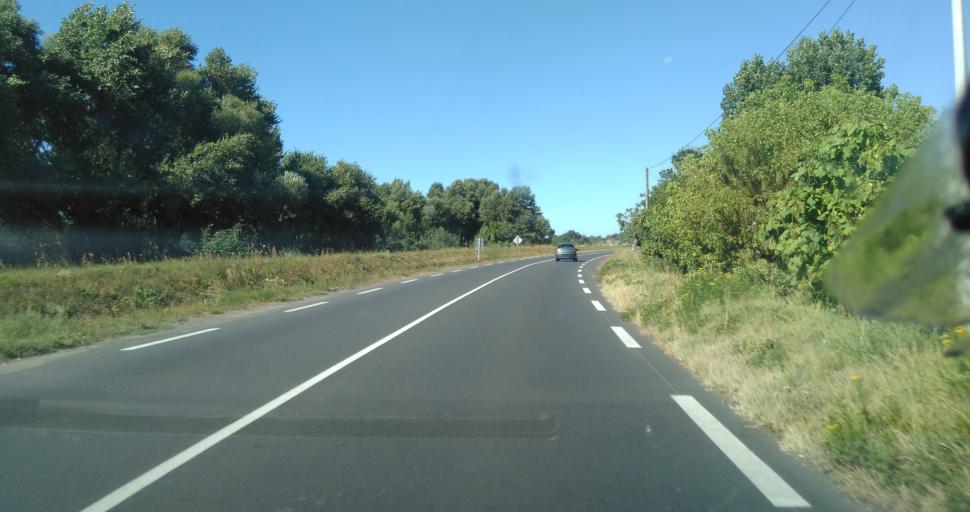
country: FR
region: Centre
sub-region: Departement d'Indre-et-Loire
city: Noizay
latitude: 47.4024
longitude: 0.9159
